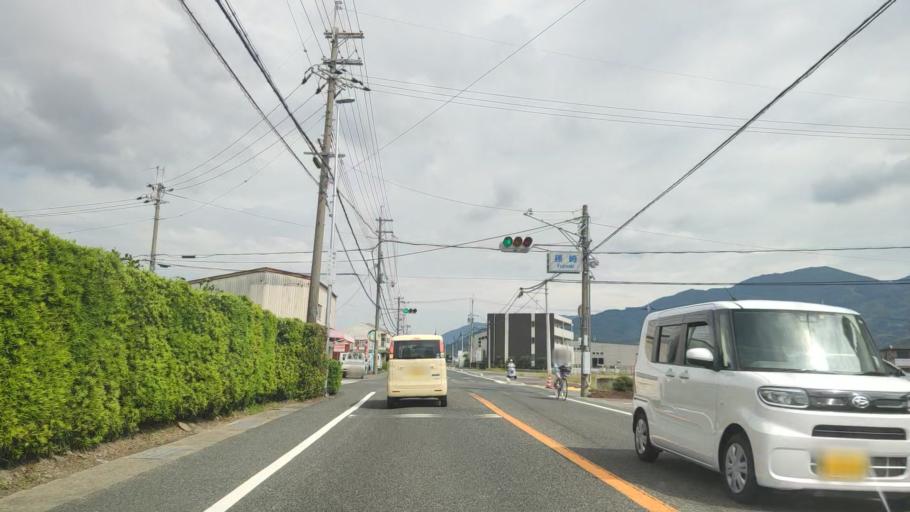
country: JP
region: Wakayama
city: Iwade
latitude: 34.2710
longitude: 135.4256
